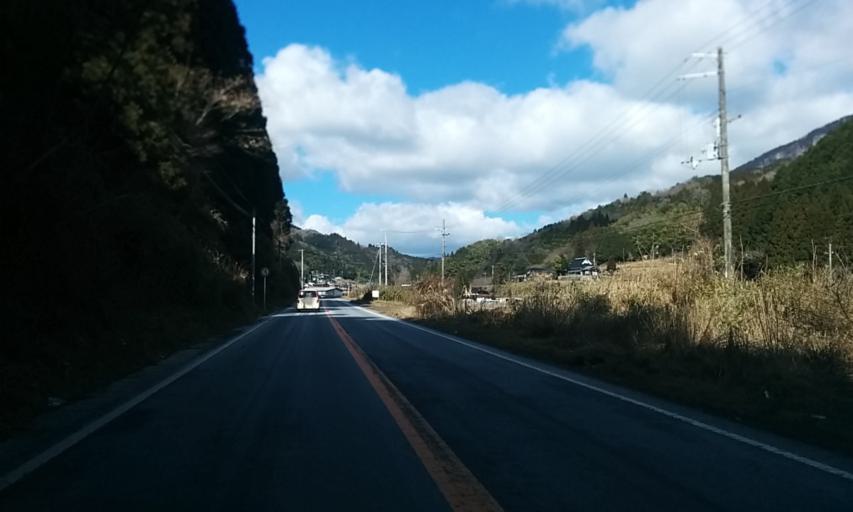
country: JP
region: Kyoto
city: Fukuchiyama
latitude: 35.3684
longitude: 135.0484
